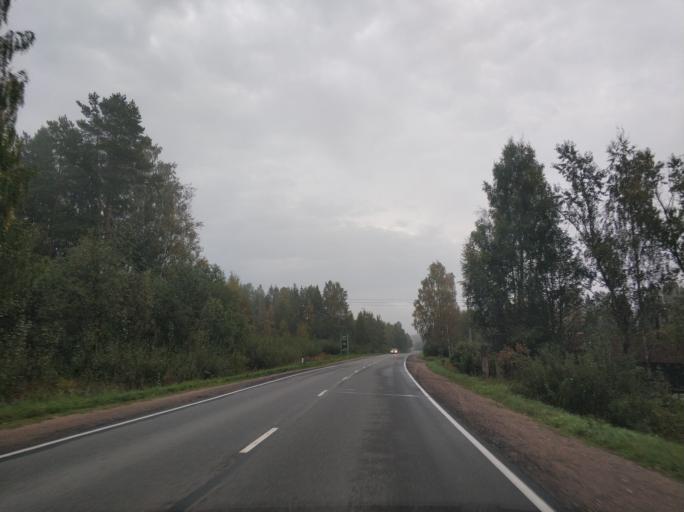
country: RU
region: Leningrad
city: Shcheglovo
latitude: 60.0974
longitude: 30.8430
